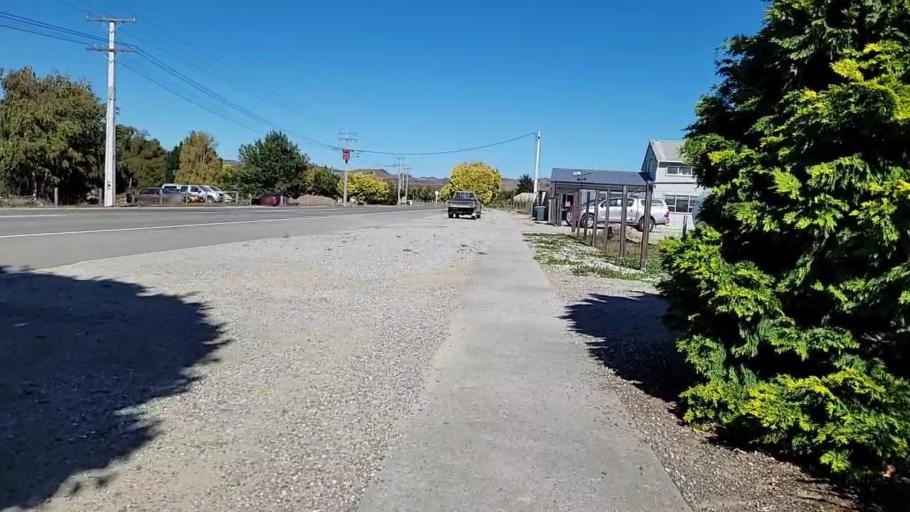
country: NZ
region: Otago
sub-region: Queenstown-Lakes District
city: Wanaka
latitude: -45.0970
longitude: 169.5988
